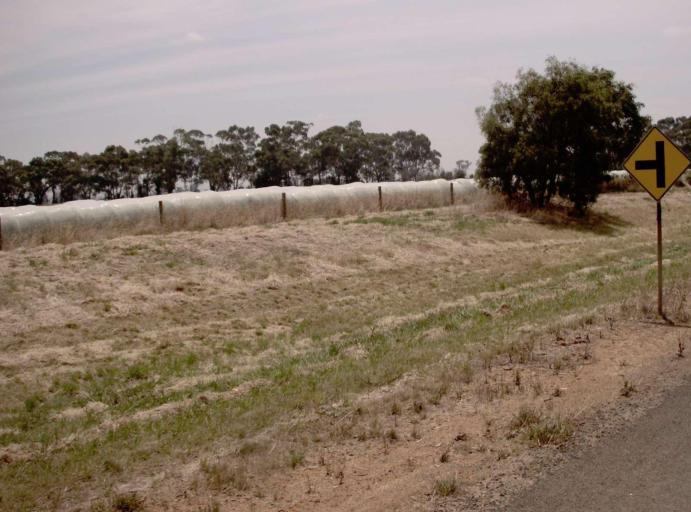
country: AU
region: Victoria
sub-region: Latrobe
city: Traralgon
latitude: -38.2428
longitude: 146.6281
